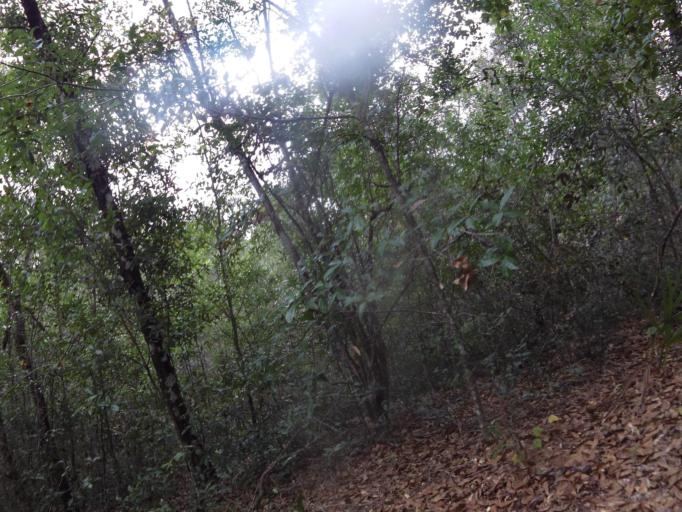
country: US
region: Florida
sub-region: Clay County
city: Keystone Heights
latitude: 29.8379
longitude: -81.9505
